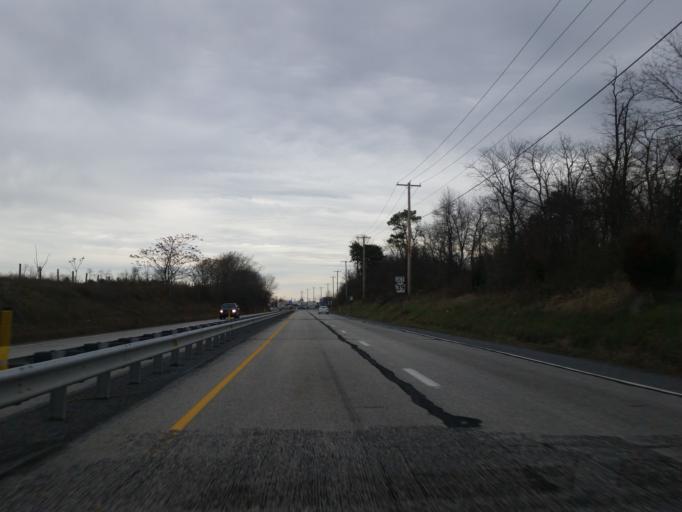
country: US
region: Pennsylvania
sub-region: Dauphin County
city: Skyline View
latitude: 40.3375
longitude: -76.7178
